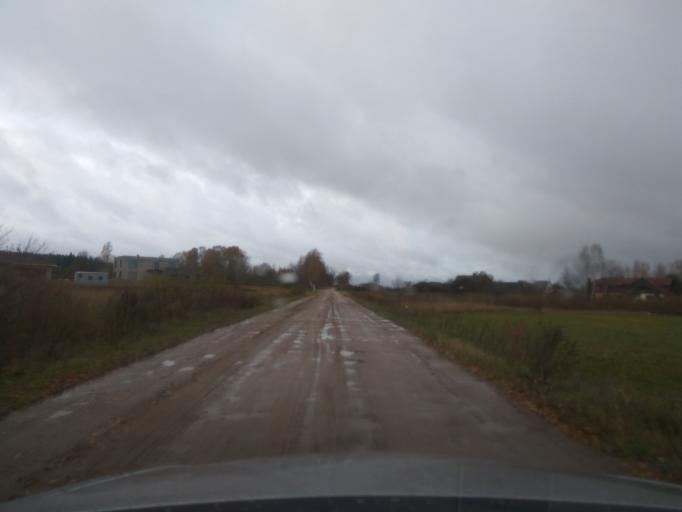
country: LV
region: Kuldigas Rajons
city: Kuldiga
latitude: 56.9692
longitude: 21.9409
